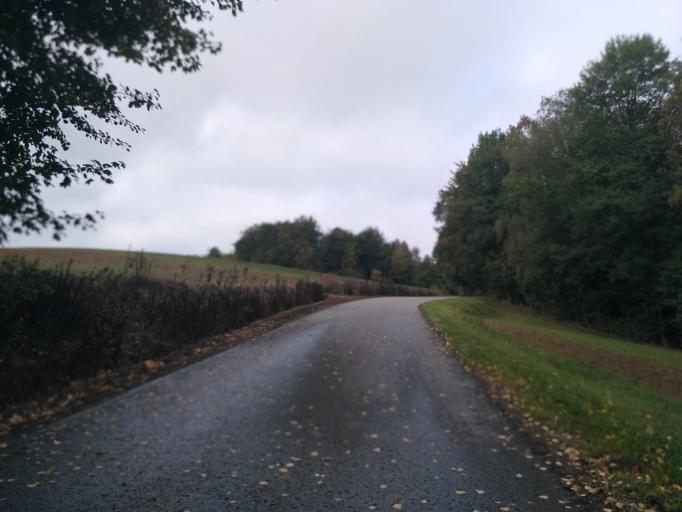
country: PL
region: Subcarpathian Voivodeship
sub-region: Powiat debicki
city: Brzostek
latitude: 49.9480
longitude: 21.4441
